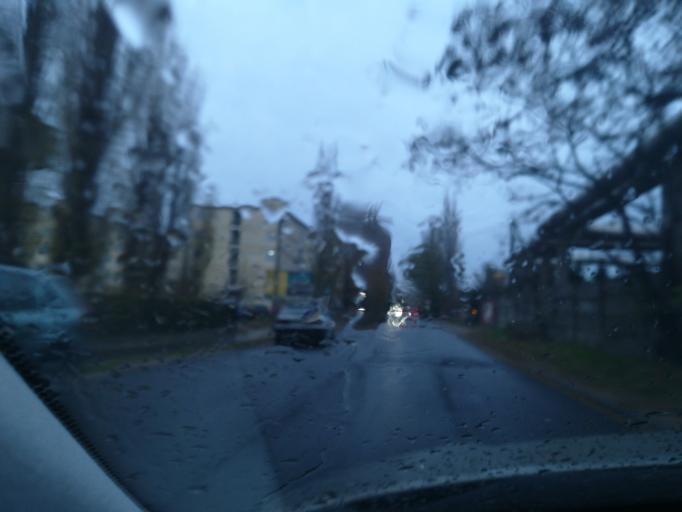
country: HU
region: Budapest
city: Budapest III. keruelet
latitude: 47.5528
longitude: 19.0338
